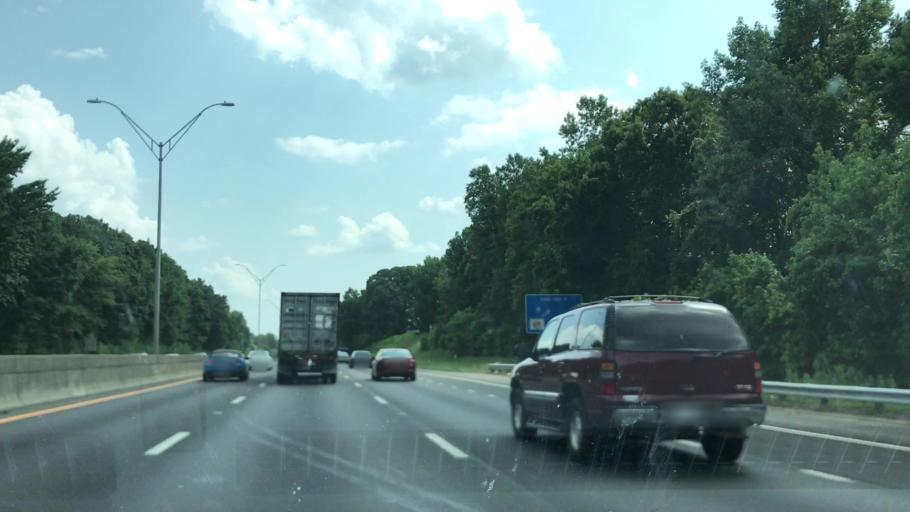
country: US
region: North Carolina
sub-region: Mecklenburg County
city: Pineville
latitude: 35.1560
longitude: -80.8925
